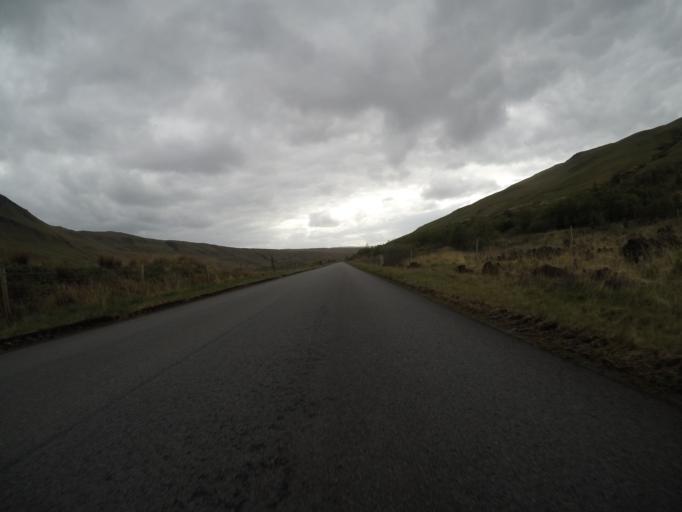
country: GB
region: Scotland
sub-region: Highland
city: Isle of Skye
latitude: 57.3010
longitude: -6.2526
